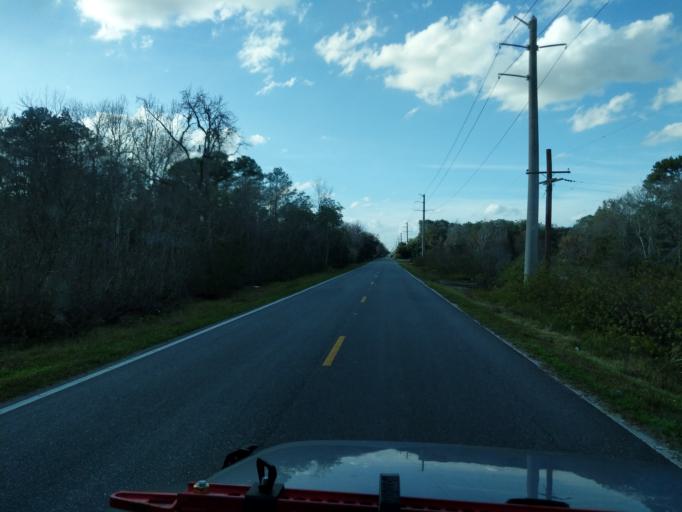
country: US
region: Florida
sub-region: Seminole County
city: Geneva
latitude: 28.7654
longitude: -81.1394
